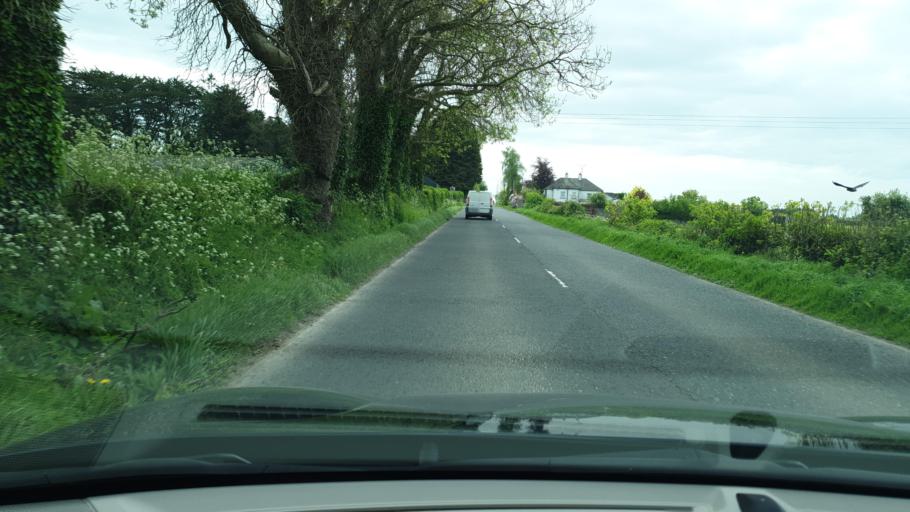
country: IE
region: Leinster
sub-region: An Mhi
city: Navan
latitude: 53.7105
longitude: -6.6896
